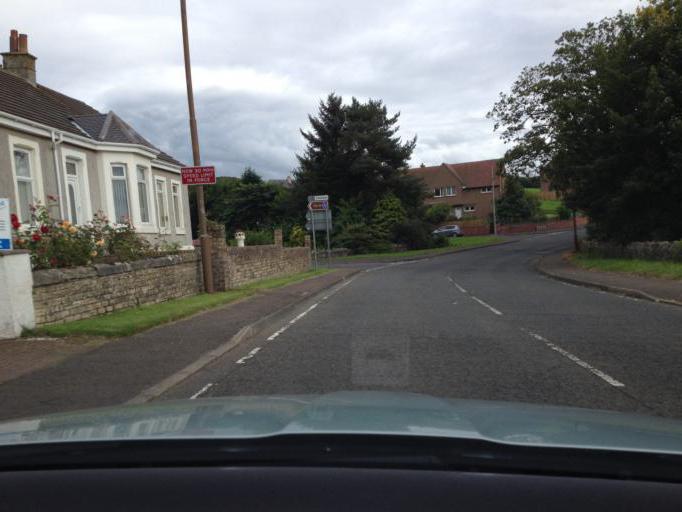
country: GB
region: Scotland
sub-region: West Lothian
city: Bathgate
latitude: 55.9139
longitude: -3.6407
